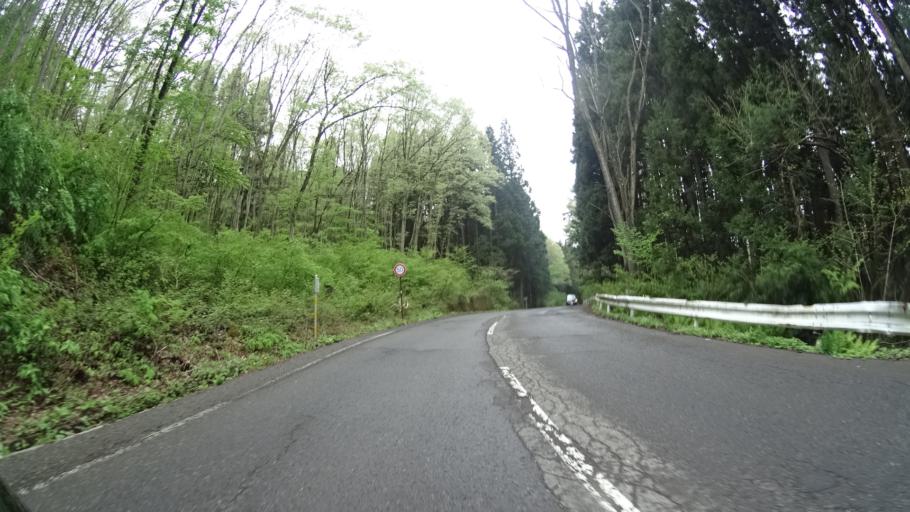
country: JP
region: Nagano
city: Nagano-shi
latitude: 36.7542
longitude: 138.2000
